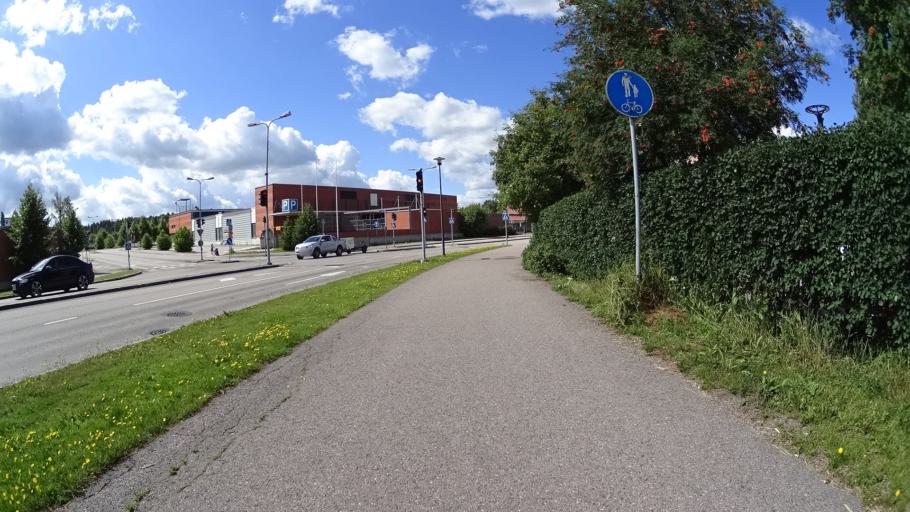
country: FI
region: Uusimaa
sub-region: Helsinki
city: Tuusula
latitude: 60.4036
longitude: 25.0297
